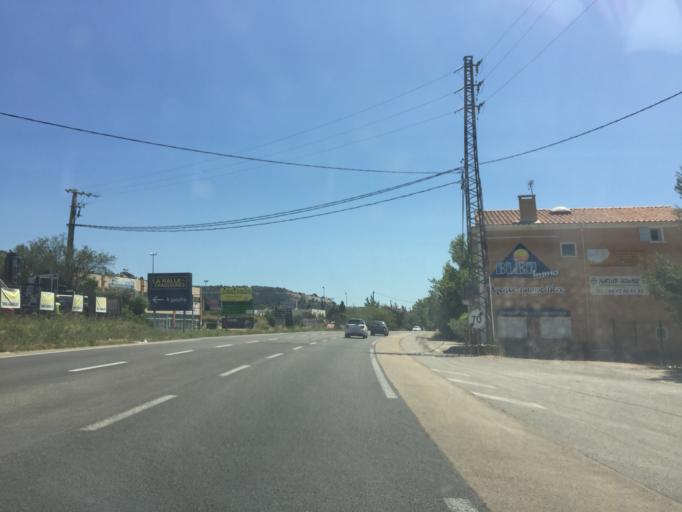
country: FR
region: Provence-Alpes-Cote d'Azur
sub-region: Departement des Bouches-du-Rhone
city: Rognac
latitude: 43.4790
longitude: 5.2273
